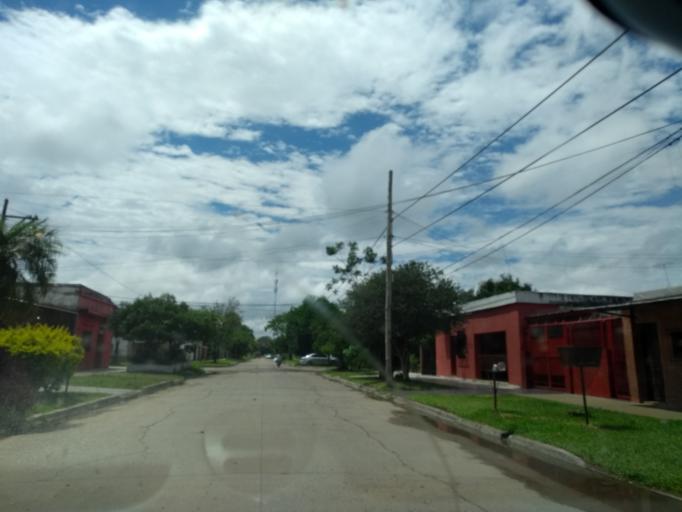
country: AR
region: Chaco
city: Barranqueras
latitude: -27.4843
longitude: -58.9420
